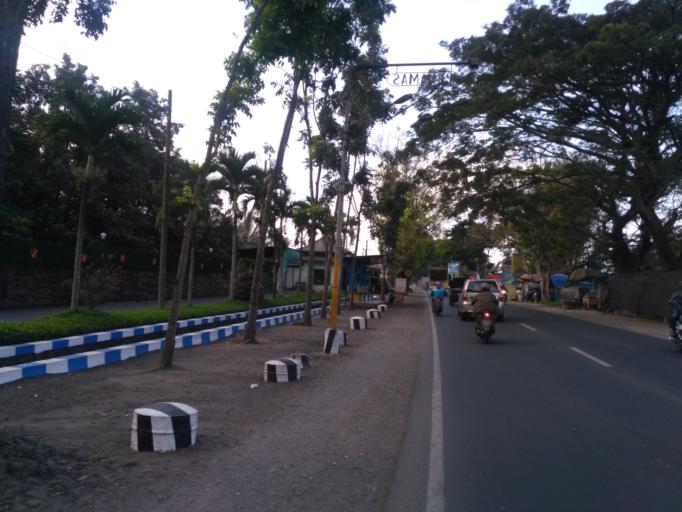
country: ID
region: East Java
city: Watudakon
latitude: -8.0347
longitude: 112.6127
